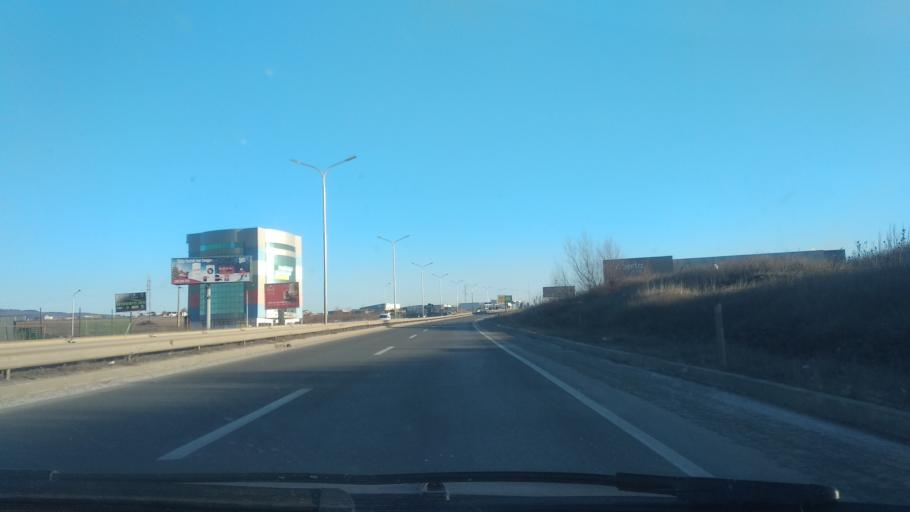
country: XK
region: Pristina
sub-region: Kosovo Polje
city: Kosovo Polje
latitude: 42.6666
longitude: 21.1243
